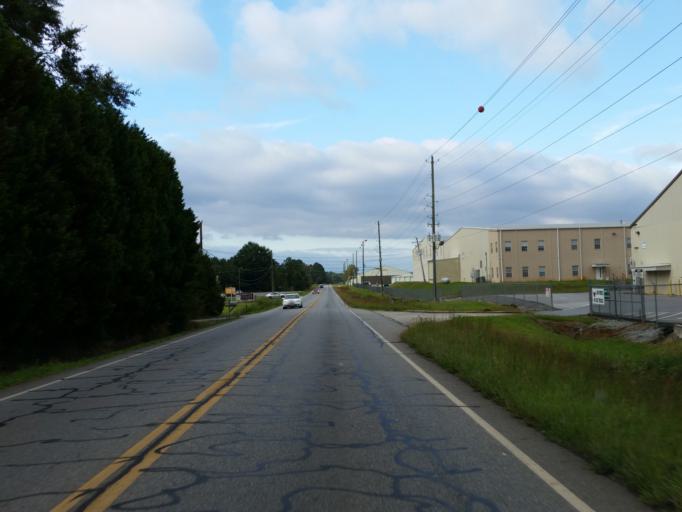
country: US
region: Georgia
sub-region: Bartow County
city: Cartersville
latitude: 34.1176
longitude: -84.8511
